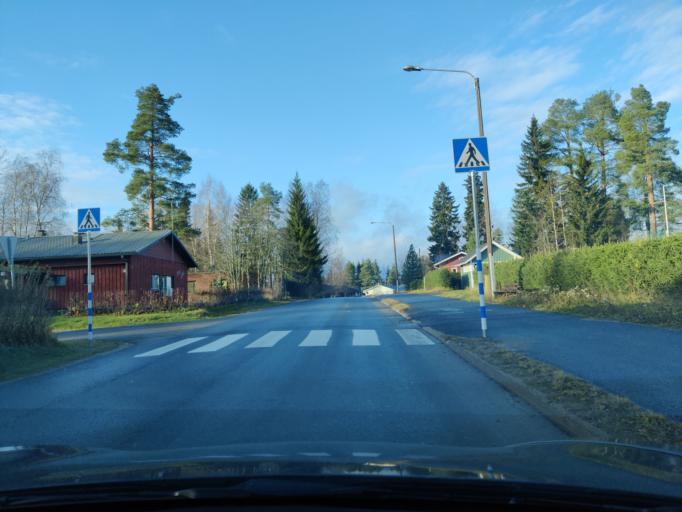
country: FI
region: Northern Savo
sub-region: Ylae-Savo
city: Kiuruvesi
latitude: 63.6452
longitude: 26.6286
